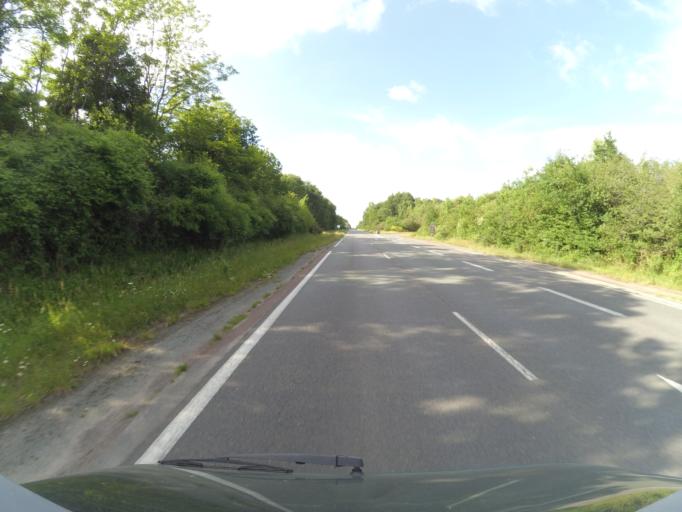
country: FR
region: Poitou-Charentes
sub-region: Departement de la Charente-Maritime
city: Le Gua
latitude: 45.7842
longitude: -0.9362
